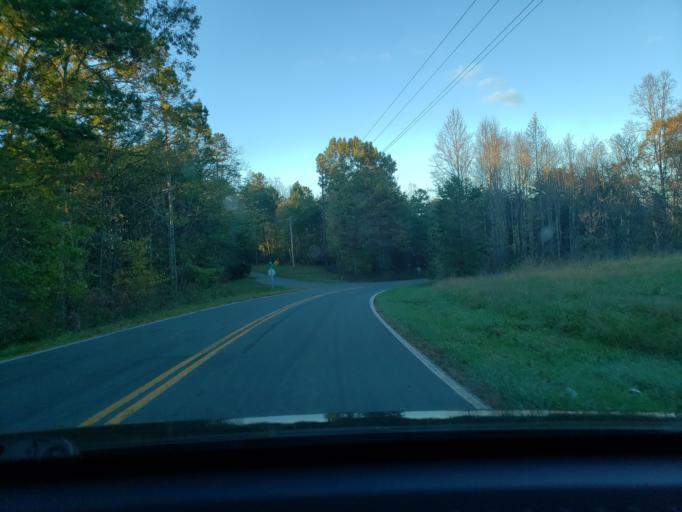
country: US
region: North Carolina
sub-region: Stokes County
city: Danbury
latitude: 36.3781
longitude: -80.1884
